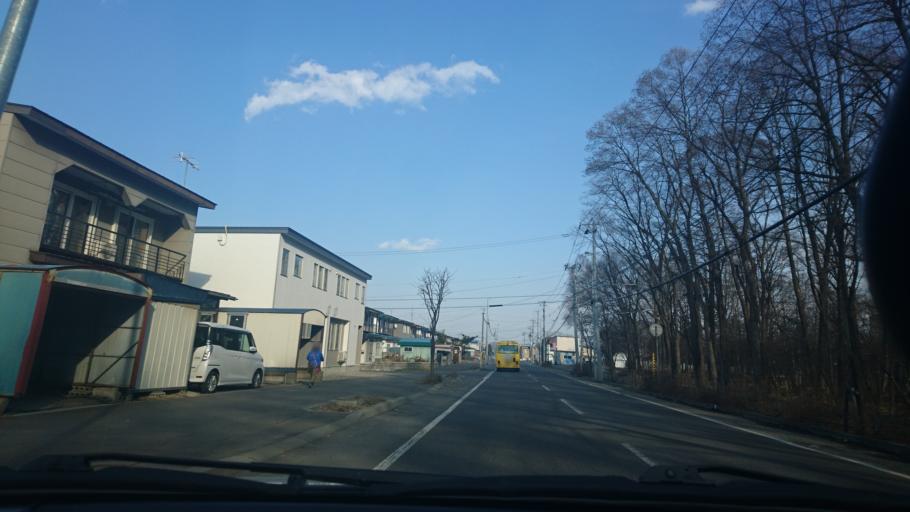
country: JP
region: Hokkaido
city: Obihiro
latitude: 42.9243
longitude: 143.1745
